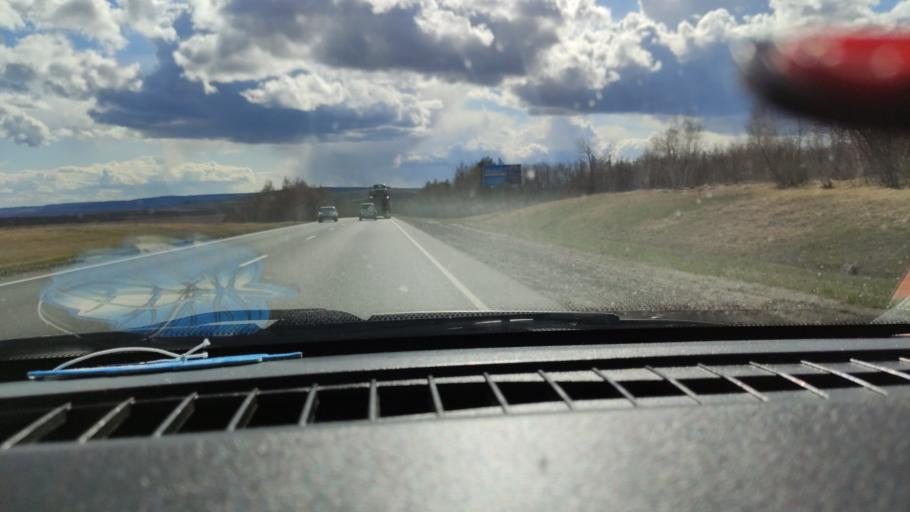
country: RU
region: Saratov
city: Khvalynsk
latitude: 52.5803
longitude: 48.1157
